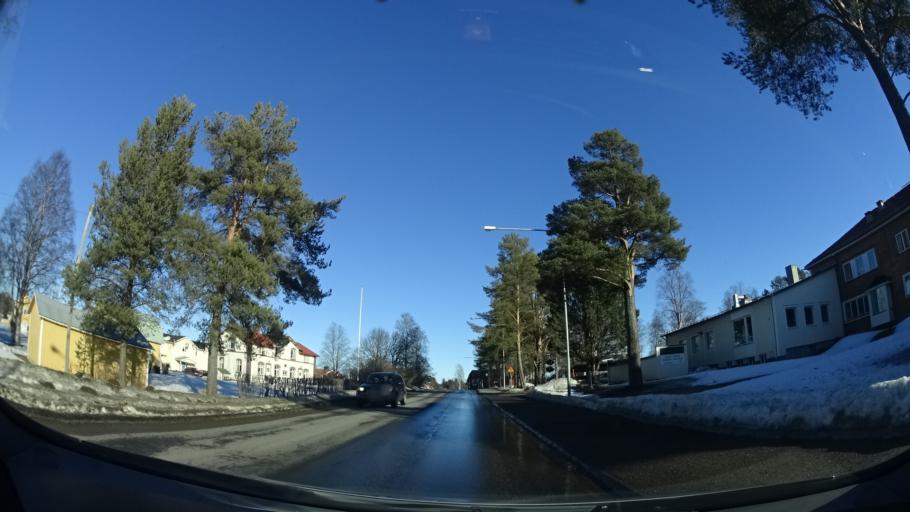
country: SE
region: Vaesterbotten
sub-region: Skelleftea Kommun
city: Byske
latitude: 64.9522
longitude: 21.1950
